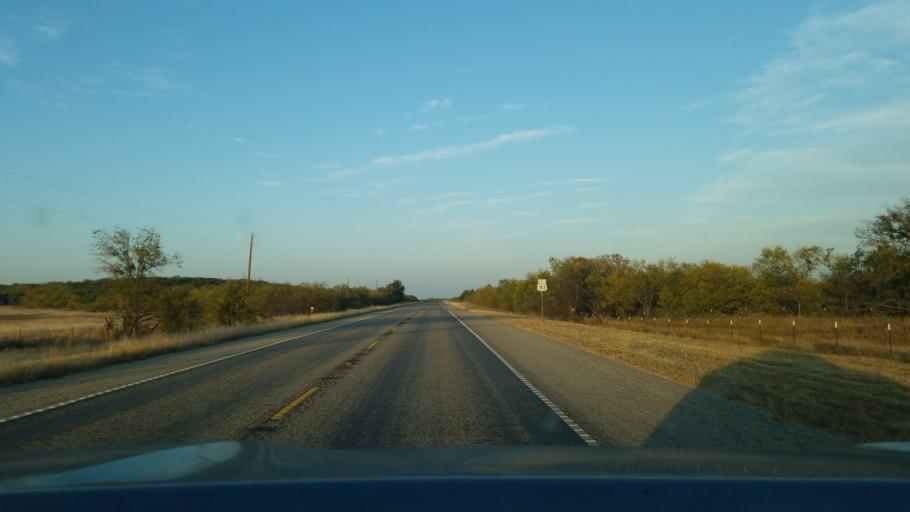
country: US
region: Texas
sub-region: Eastland County
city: Cisco
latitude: 32.4388
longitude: -98.9188
